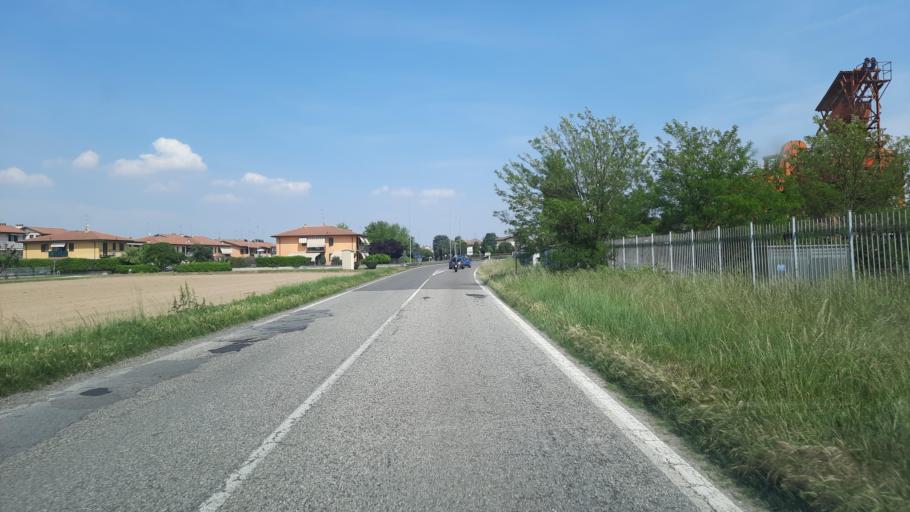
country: IT
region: Lombardy
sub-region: Provincia di Pavia
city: Carbonara al Ticino
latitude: 45.1640
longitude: 9.0532
